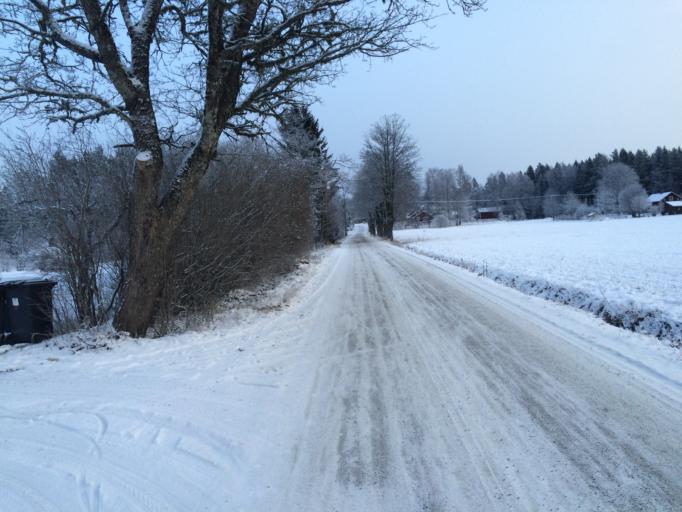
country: SE
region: Uppsala
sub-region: Enkopings Kommun
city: Orsundsbro
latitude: 59.9087
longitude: 17.2053
